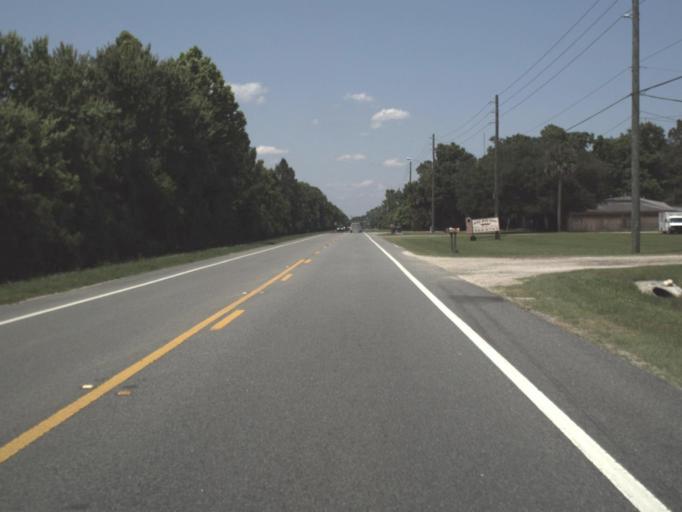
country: US
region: Florida
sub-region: Nassau County
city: Yulee
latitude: 30.5091
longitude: -81.6228
